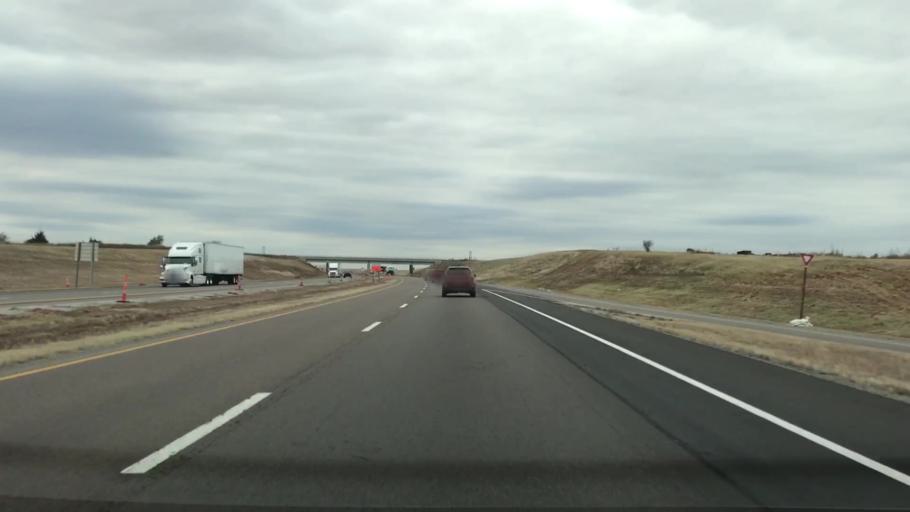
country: US
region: Oklahoma
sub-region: Beckham County
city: Elk City
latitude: 35.4264
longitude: -99.2792
